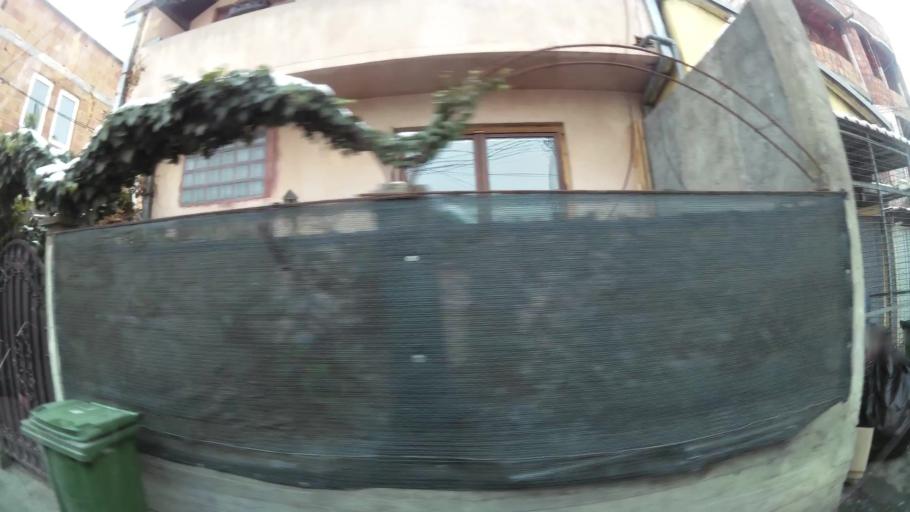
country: MK
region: Cair
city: Cair
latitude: 42.0104
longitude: 21.4382
